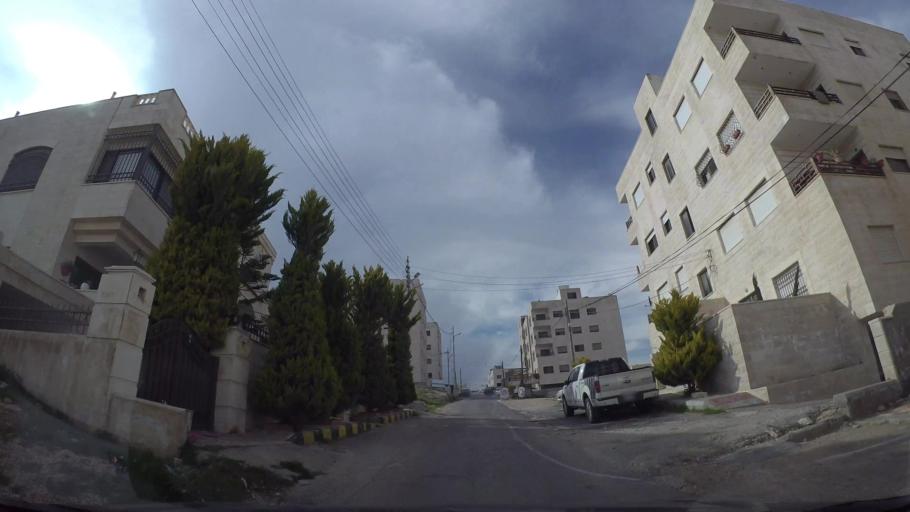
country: JO
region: Amman
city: Amman
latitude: 32.0116
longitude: 35.9392
